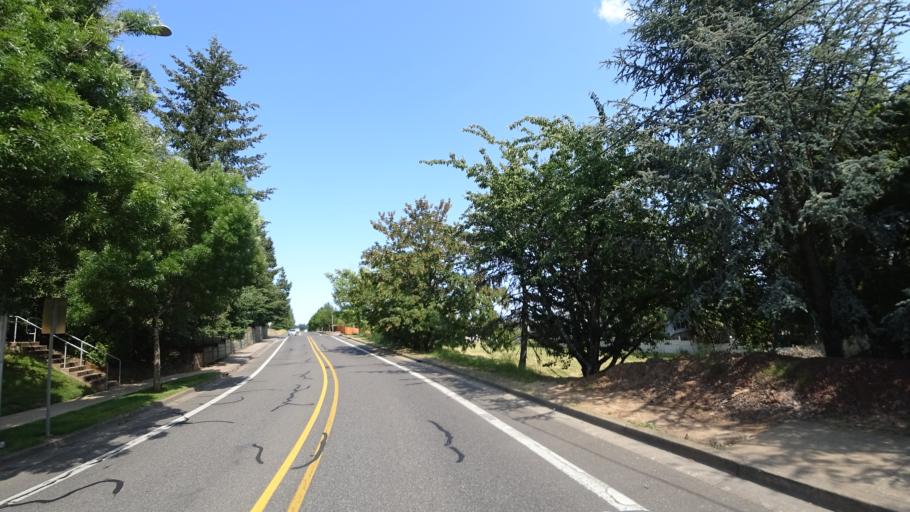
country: US
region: Oregon
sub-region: Clackamas County
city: Happy Valley
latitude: 45.4398
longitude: -122.5486
